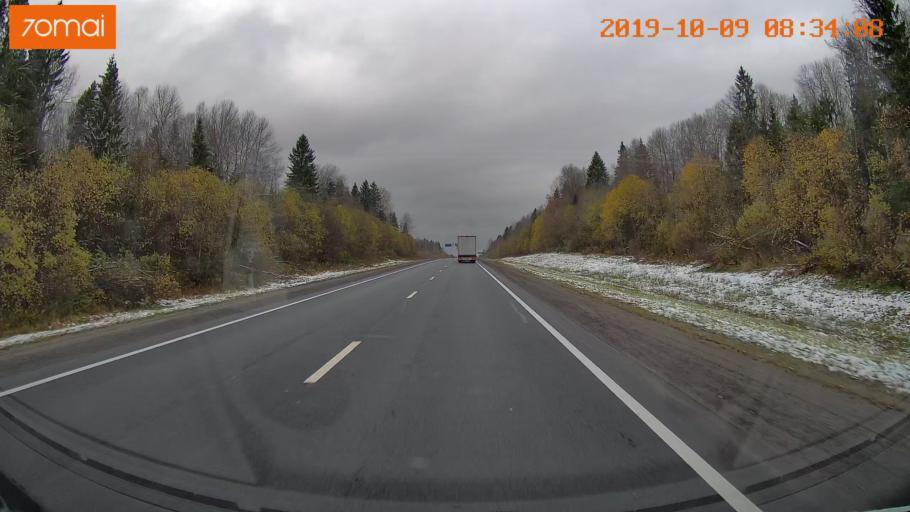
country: RU
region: Vologda
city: Gryazovets
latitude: 58.8925
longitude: 40.1875
